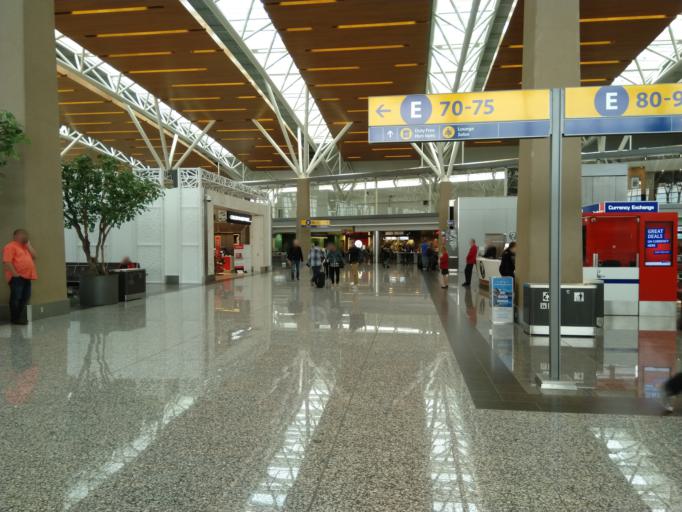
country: CA
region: Alberta
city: Calgary
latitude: 51.1299
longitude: -114.0035
